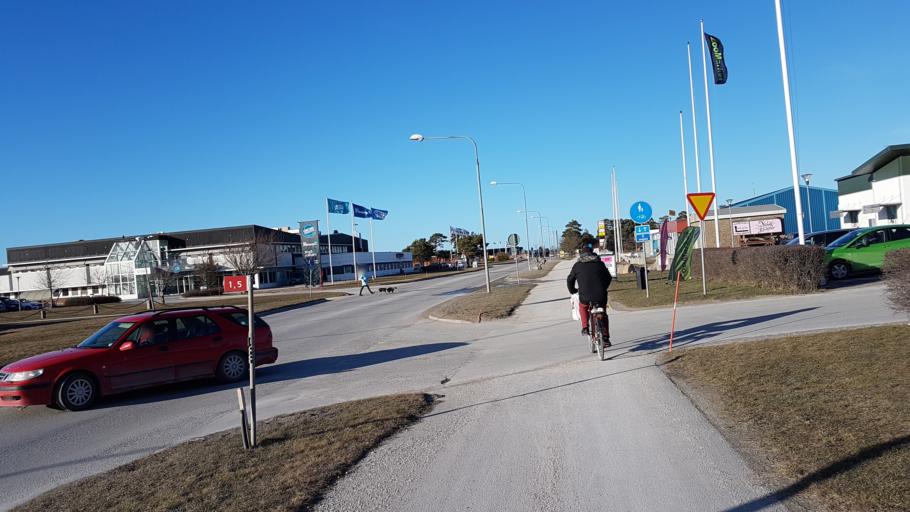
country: SE
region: Gotland
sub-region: Gotland
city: Visby
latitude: 57.6357
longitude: 18.3267
